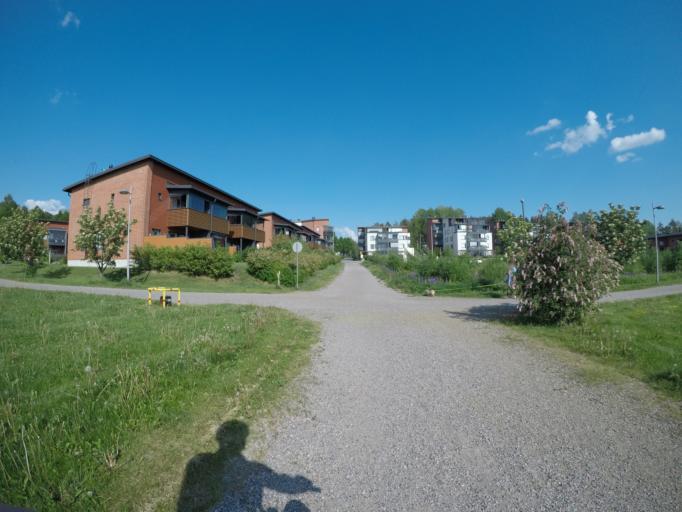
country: FI
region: Haeme
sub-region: Haemeenlinna
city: Haemeenlinna
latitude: 61.0110
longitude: 24.4628
